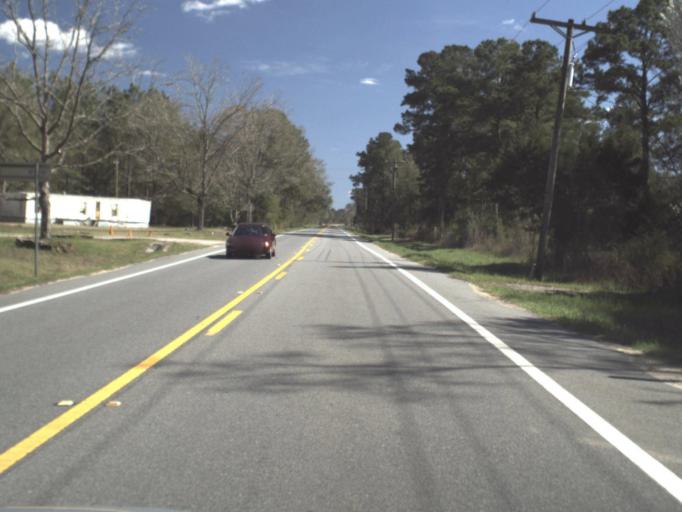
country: US
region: Florida
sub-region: Gadsden County
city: Gretna
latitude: 30.6570
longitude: -84.6906
